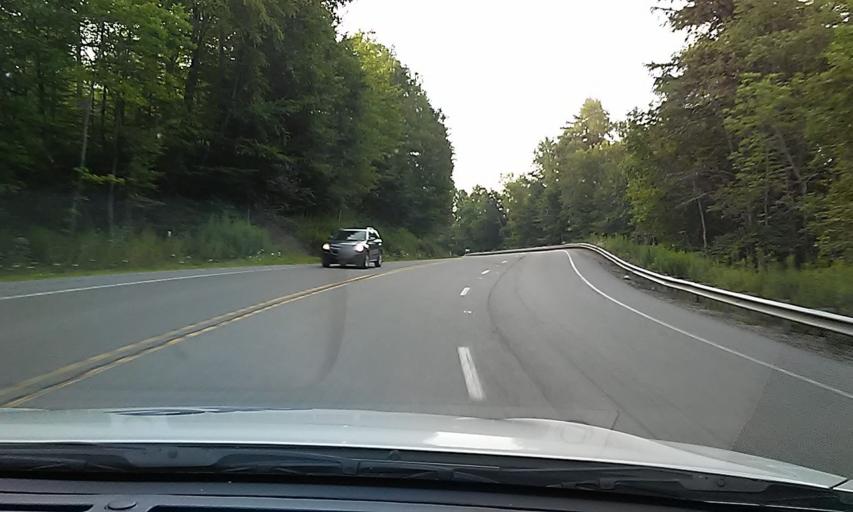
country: US
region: Pennsylvania
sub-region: McKean County
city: Smethport
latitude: 41.7185
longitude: -78.6113
